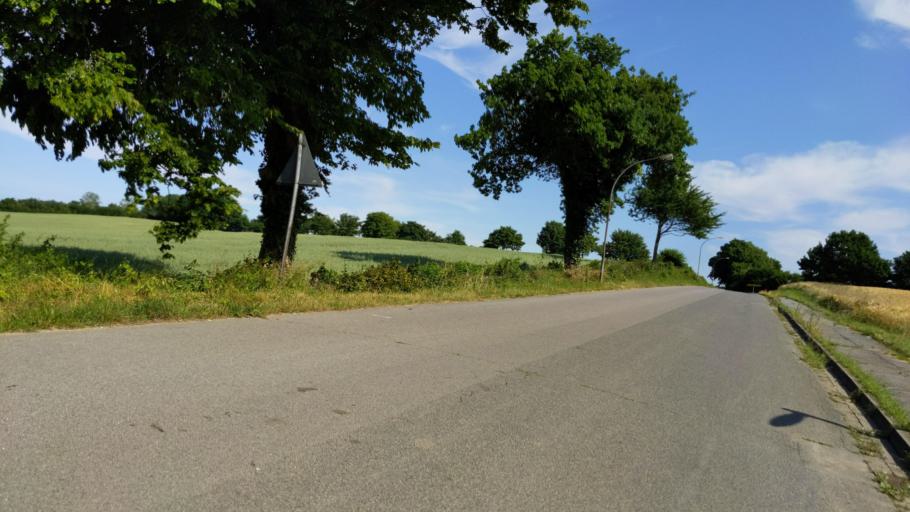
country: DE
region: Schleswig-Holstein
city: Scharbeutz
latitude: 54.0175
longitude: 10.7106
